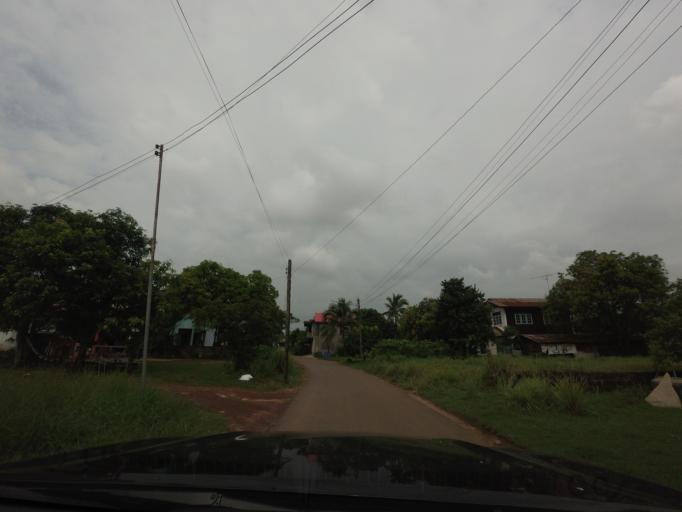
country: TH
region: Nong Khai
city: Nong Khai
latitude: 17.8173
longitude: 102.7030
